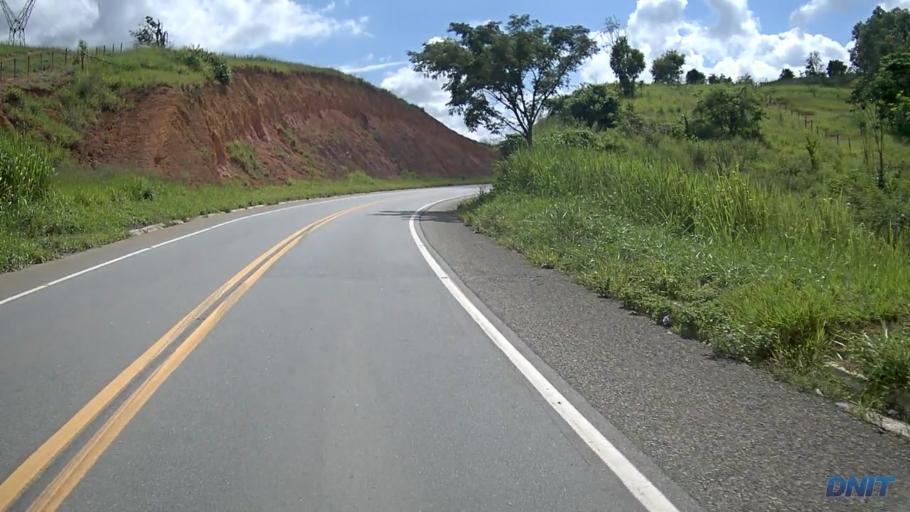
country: BR
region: Minas Gerais
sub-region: Belo Oriente
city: Belo Oriente
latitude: -19.0934
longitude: -42.1933
